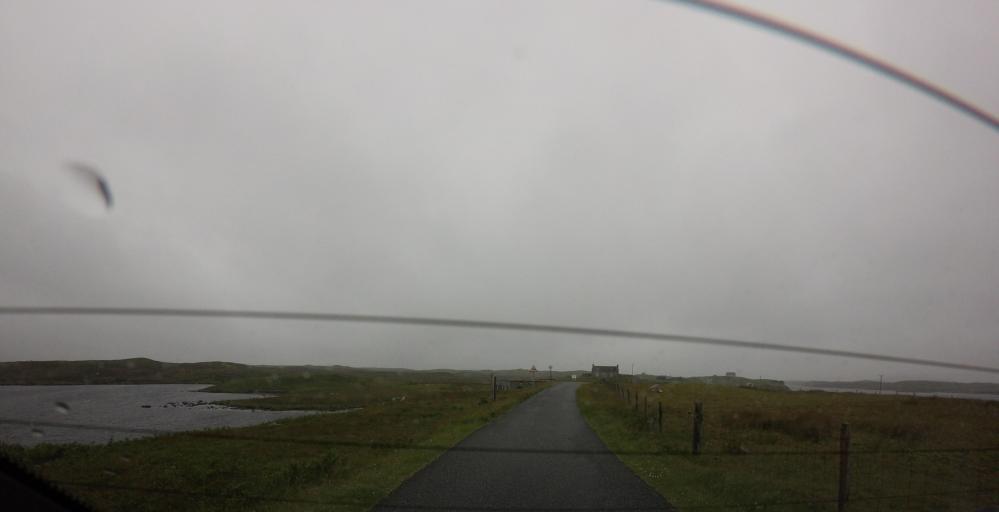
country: GB
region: Scotland
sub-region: Eilean Siar
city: Isle of North Uist
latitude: 57.5508
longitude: -7.2160
